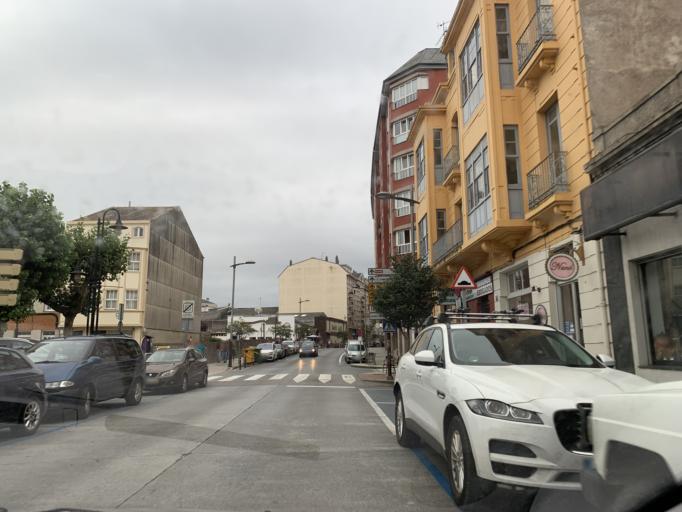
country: ES
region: Galicia
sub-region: Provincia de Lugo
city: Ribadeo
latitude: 43.5357
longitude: -7.0432
